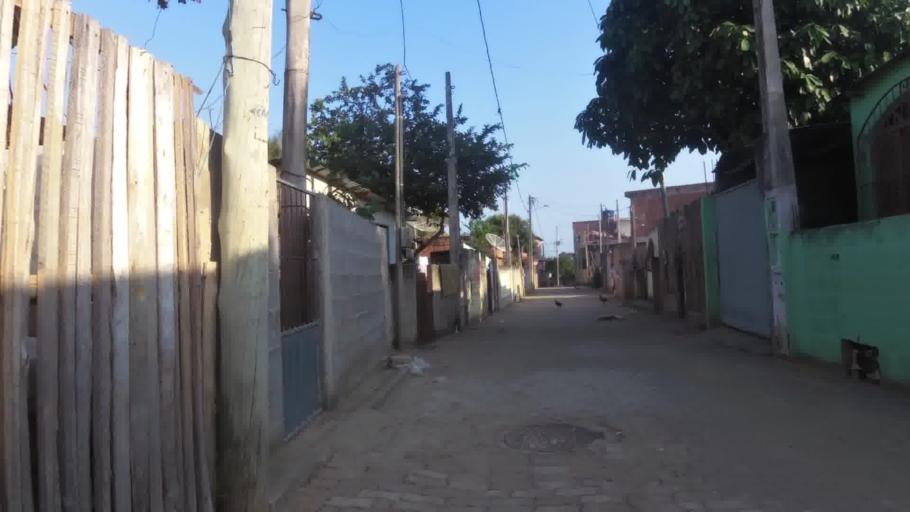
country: BR
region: Espirito Santo
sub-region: Piuma
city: Piuma
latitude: -20.8223
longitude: -40.7191
